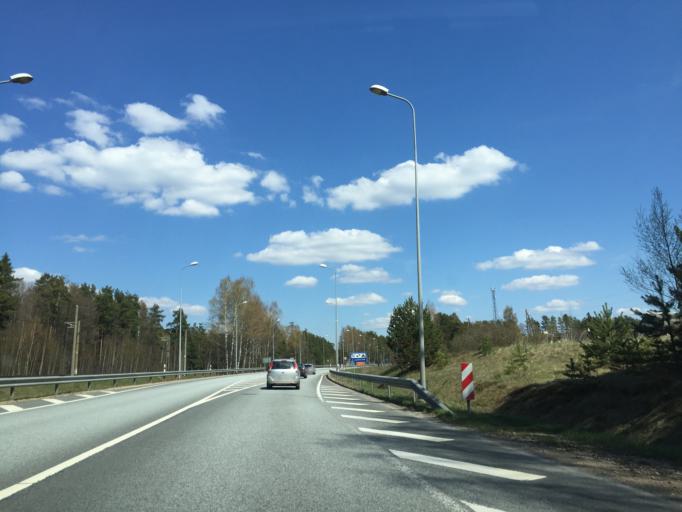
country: LV
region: Carnikava
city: Carnikava
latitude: 57.1896
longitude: 24.3480
